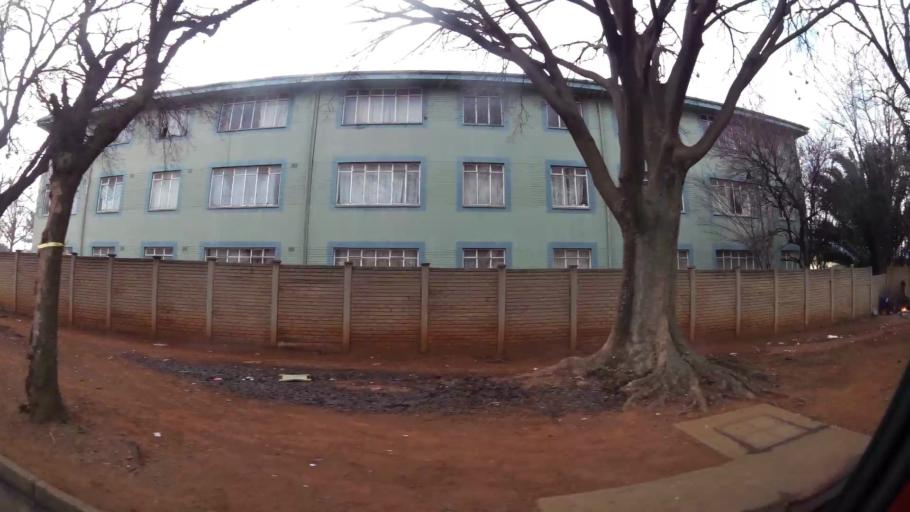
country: ZA
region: Gauteng
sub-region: Sedibeng District Municipality
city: Vanderbijlpark
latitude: -26.6958
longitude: 27.8221
